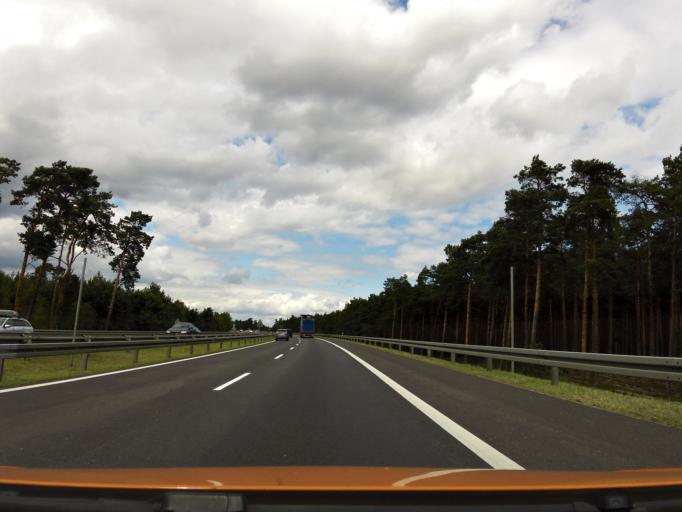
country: PL
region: West Pomeranian Voivodeship
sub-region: Powiat goleniowski
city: Goleniow
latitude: 53.5272
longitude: 14.8111
